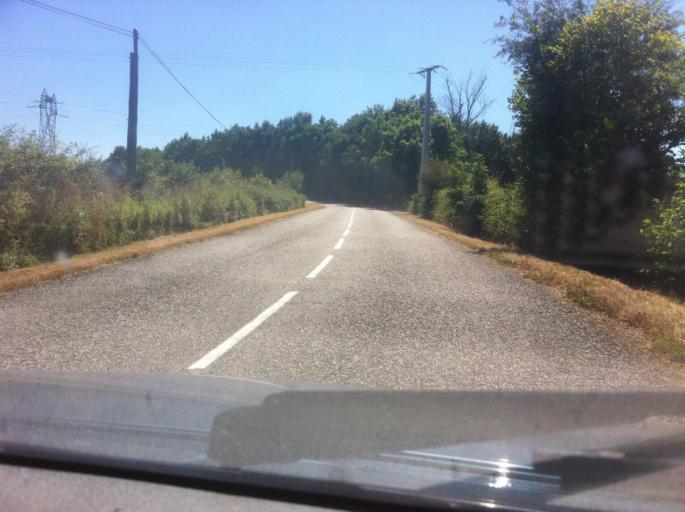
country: FR
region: Auvergne
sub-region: Departement de l'Allier
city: Montmarault
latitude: 46.3027
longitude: 3.0250
